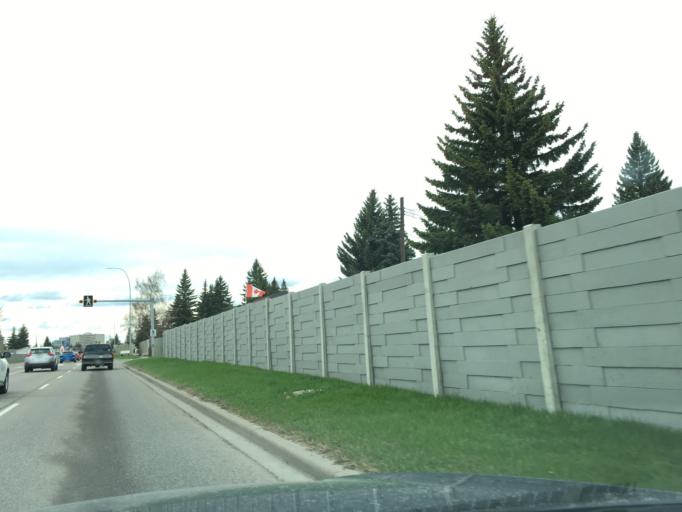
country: CA
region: Alberta
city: Calgary
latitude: 50.9641
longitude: -114.0512
